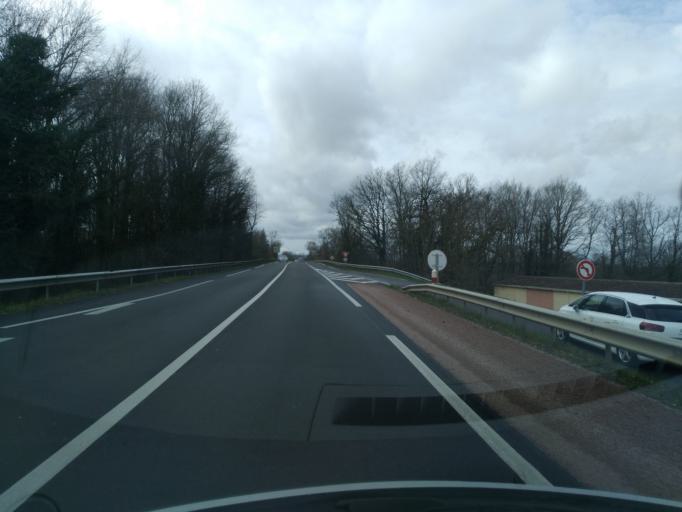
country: FR
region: Bourgogne
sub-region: Departement de Saone-et-Loire
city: Montchanin
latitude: 46.7574
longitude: 4.4750
